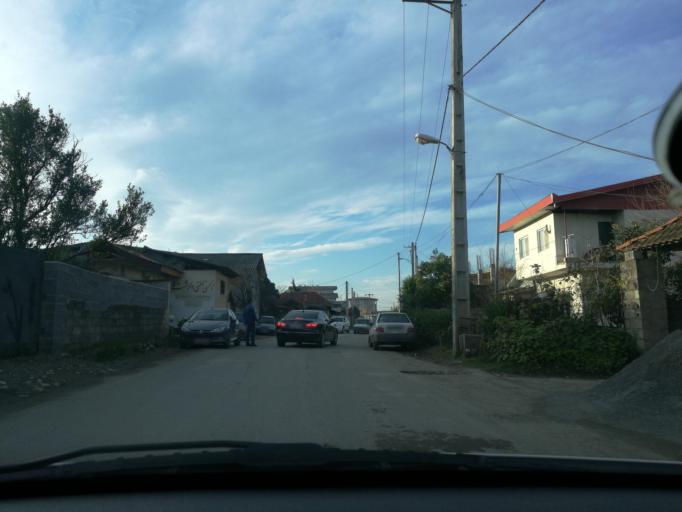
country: IR
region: Mazandaran
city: Chalus
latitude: 36.6392
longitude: 51.4444
